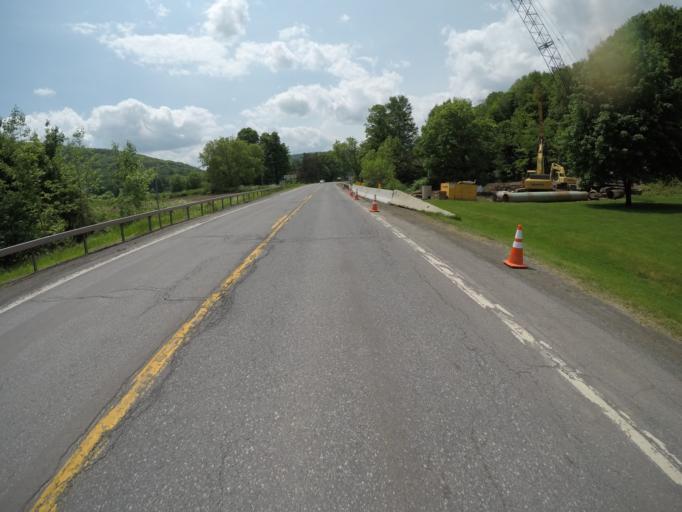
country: US
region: New York
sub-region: Delaware County
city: Stamford
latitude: 42.1508
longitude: -74.6373
